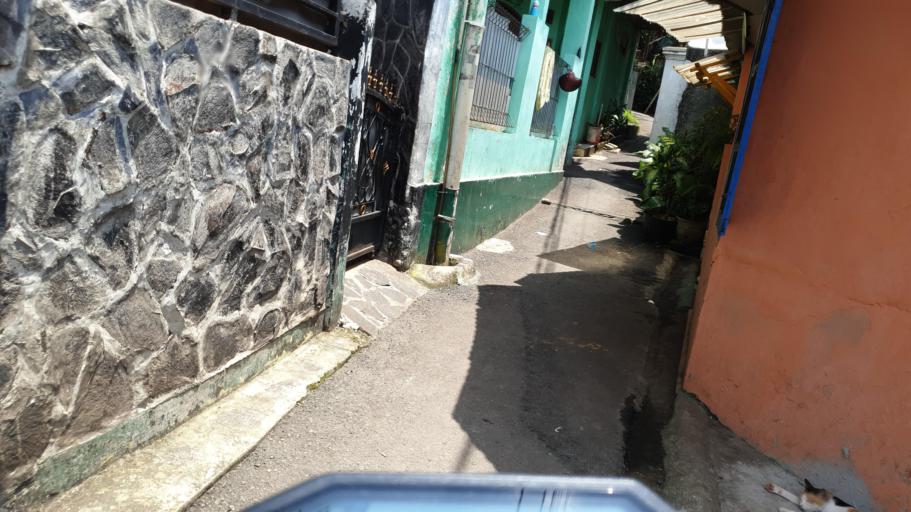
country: ID
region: West Java
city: Depok
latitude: -6.3275
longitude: 106.8301
